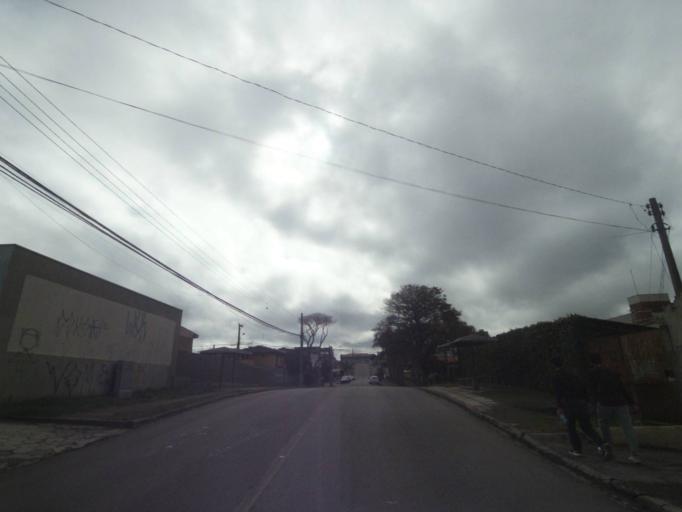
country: BR
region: Parana
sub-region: Curitiba
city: Curitiba
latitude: -25.5028
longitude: -49.2852
